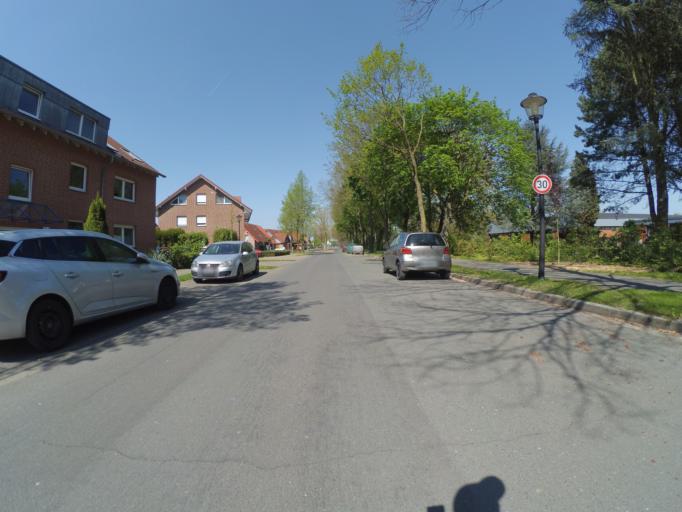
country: DE
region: North Rhine-Westphalia
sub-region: Regierungsbezirk Munster
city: Nordkirchen
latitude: 51.7431
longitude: 7.5270
